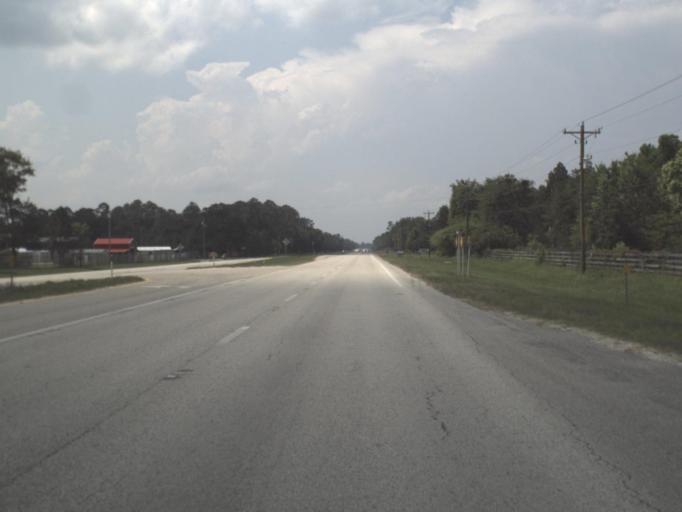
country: US
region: Florida
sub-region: Clay County
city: Green Cove Springs
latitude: 29.9060
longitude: -81.6760
